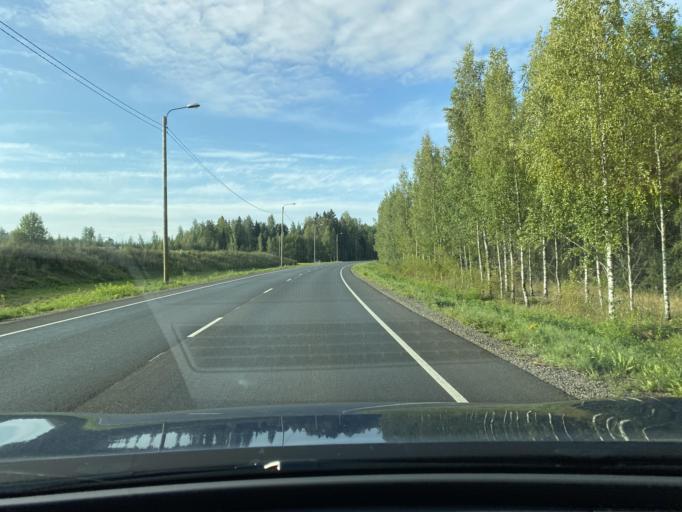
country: FI
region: Kymenlaakso
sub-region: Kouvola
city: Kouvola
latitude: 60.8871
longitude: 26.6045
